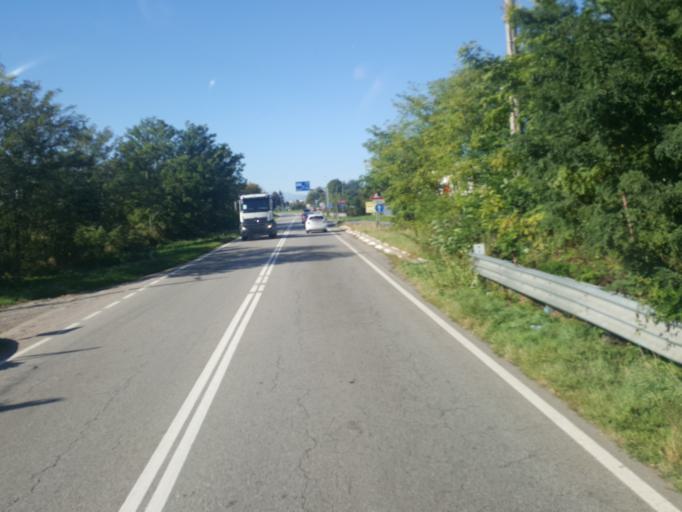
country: IT
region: Lombardy
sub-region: Citta metropolitana di Milano
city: Arluno
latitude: 45.4914
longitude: 8.9372
